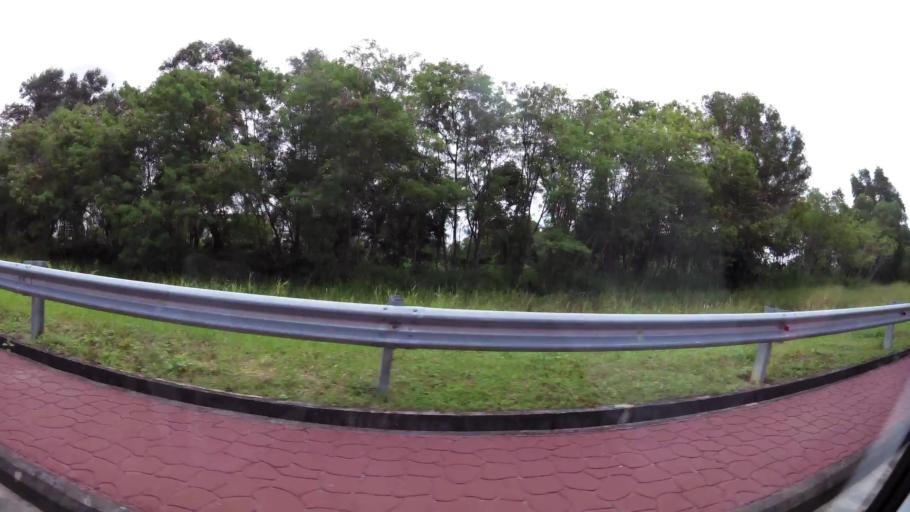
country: BN
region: Brunei and Muara
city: Bandar Seri Begawan
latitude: 4.9178
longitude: 114.9266
